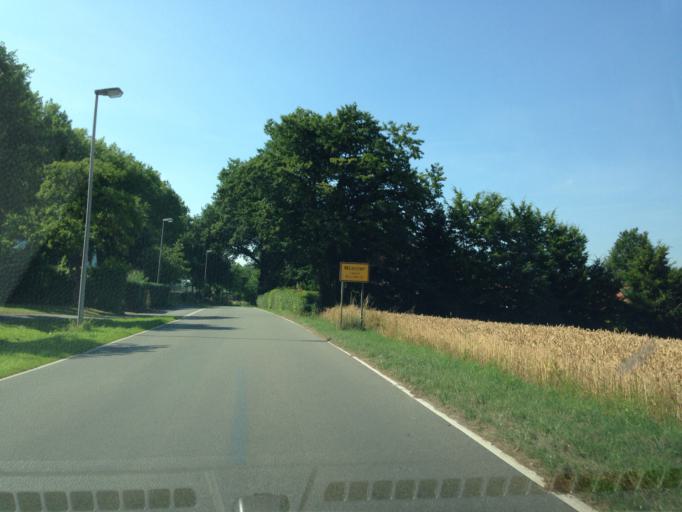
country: DE
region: North Rhine-Westphalia
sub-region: Regierungsbezirk Munster
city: Muenster
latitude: 51.9610
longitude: 7.5786
